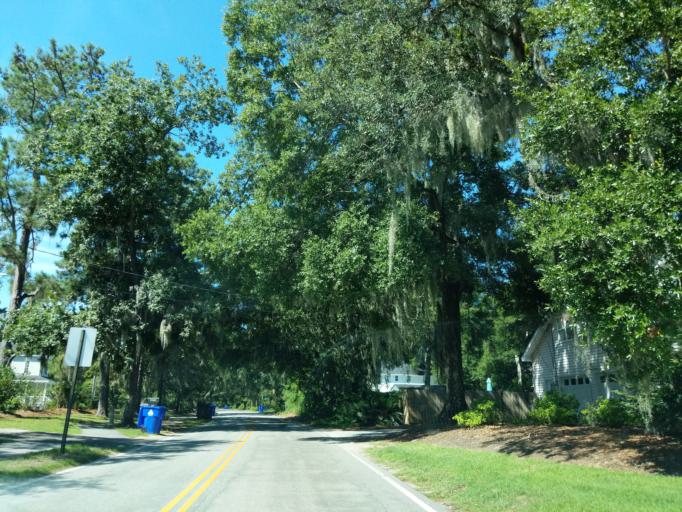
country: US
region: South Carolina
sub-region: Charleston County
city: Charleston
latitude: 32.7462
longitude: -79.9090
